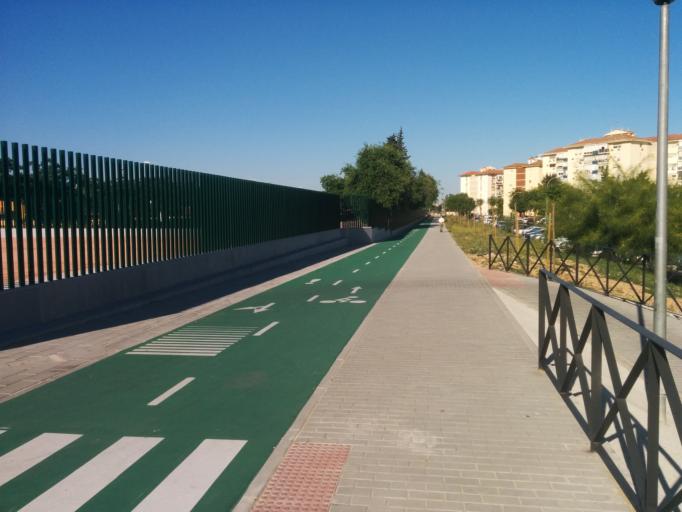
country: ES
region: Andalusia
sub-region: Provincia de Sevilla
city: Sevilla
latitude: 37.4075
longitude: -5.9195
